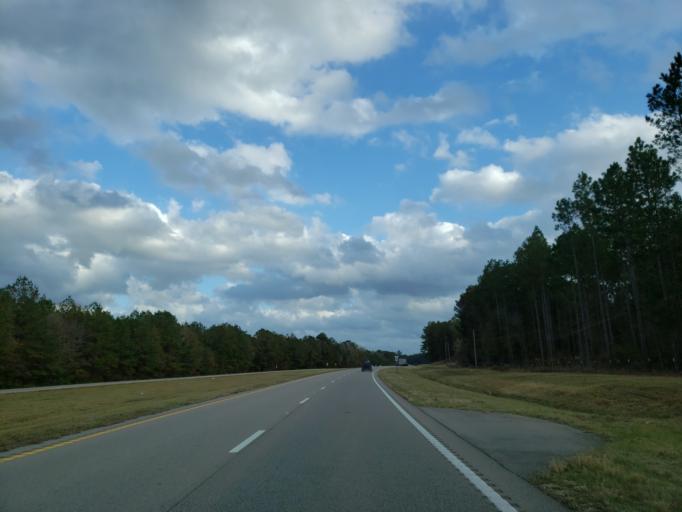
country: US
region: Mississippi
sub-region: Forrest County
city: Hattiesburg
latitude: 31.2399
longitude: -89.2167
